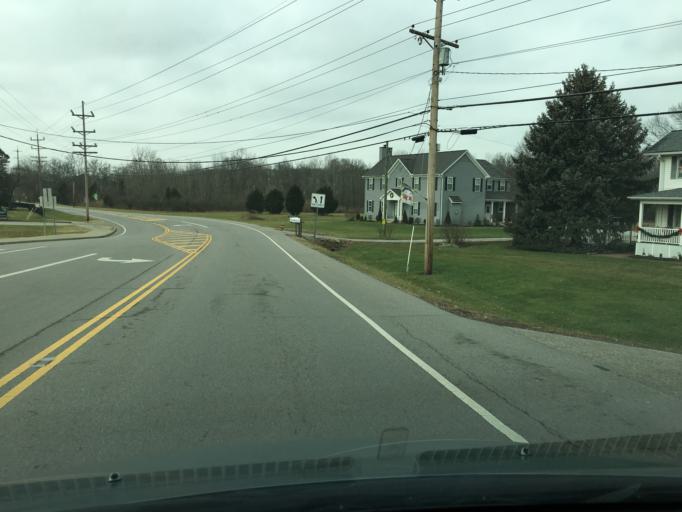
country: US
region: Ohio
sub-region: Butler County
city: Beckett Ridge
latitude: 39.3255
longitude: -84.4112
